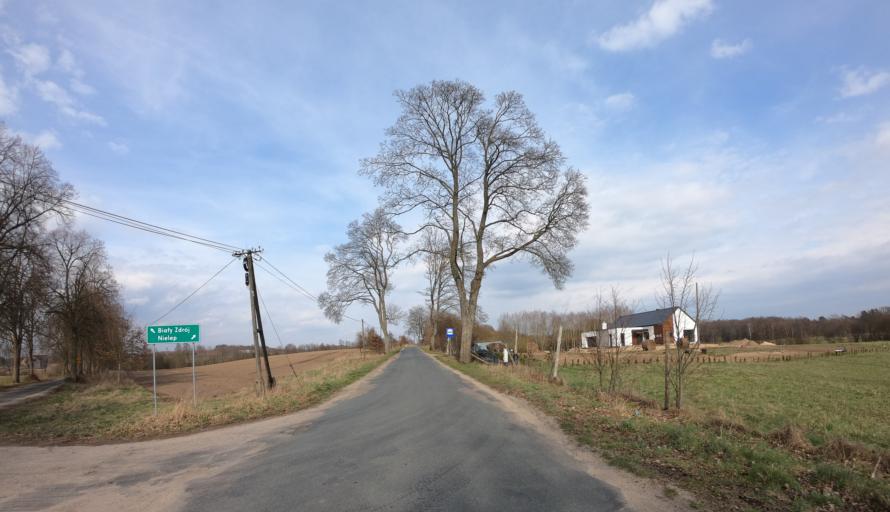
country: PL
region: West Pomeranian Voivodeship
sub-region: Powiat swidwinski
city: Swidwin
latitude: 53.8152
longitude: 15.7949
